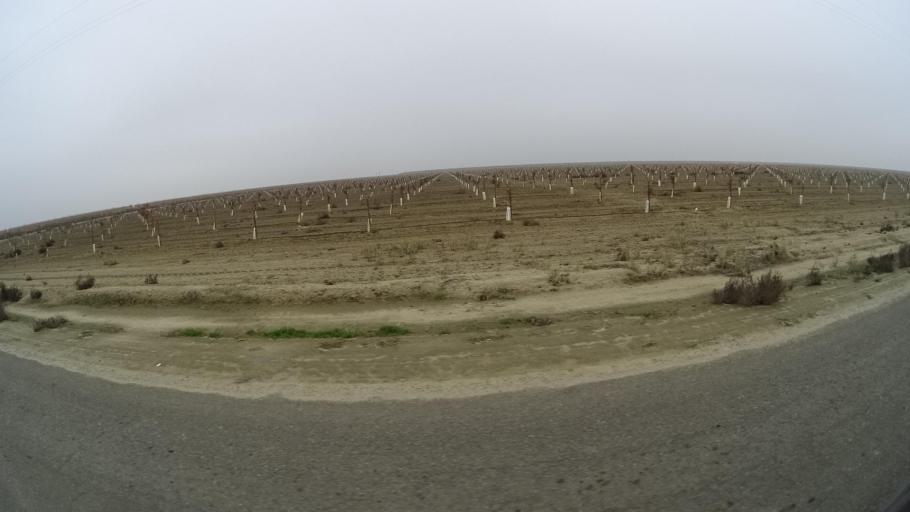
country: US
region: California
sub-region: Kern County
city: Wasco
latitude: 35.6950
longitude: -119.4195
